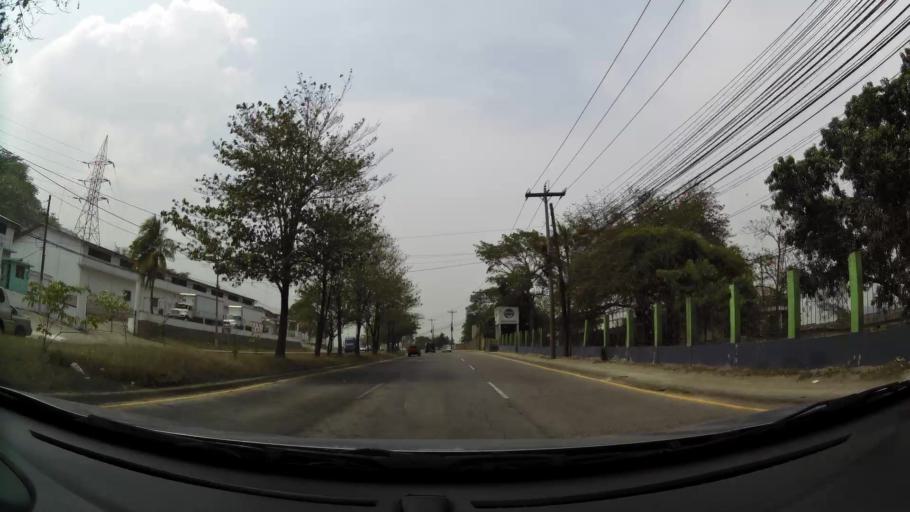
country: HN
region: Cortes
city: Chotepe
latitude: 15.4420
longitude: -88.0206
